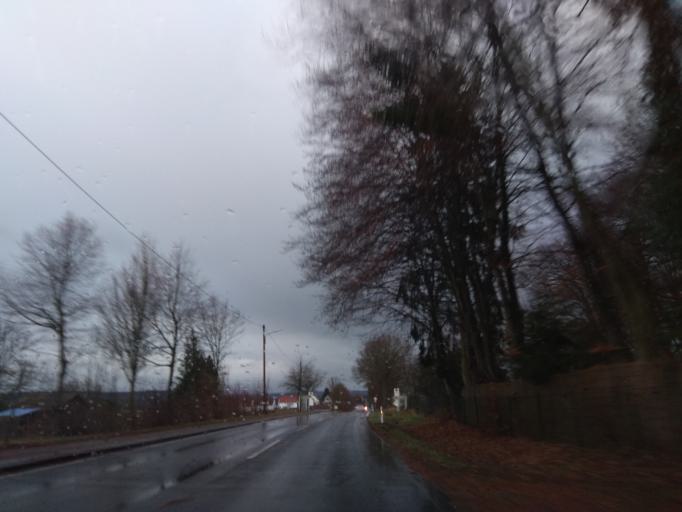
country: DE
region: Baden-Wuerttemberg
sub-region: Regierungsbezirk Stuttgart
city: Steinenbronn
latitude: 48.7006
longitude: 9.1173
